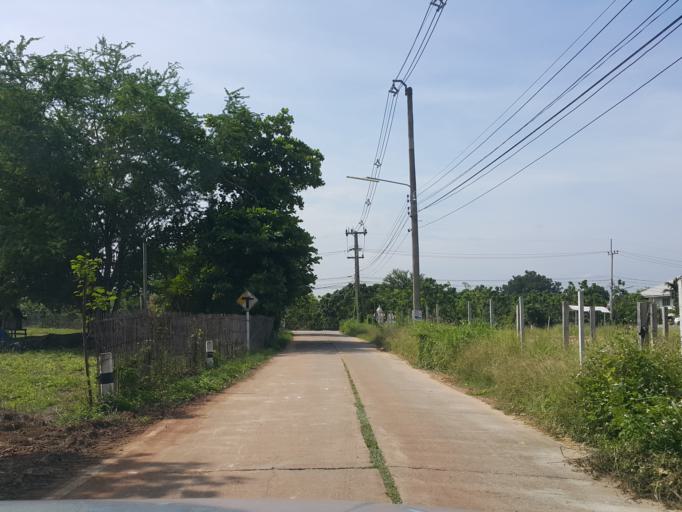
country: TH
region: Chiang Mai
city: Saraphi
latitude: 18.6837
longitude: 99.0682
